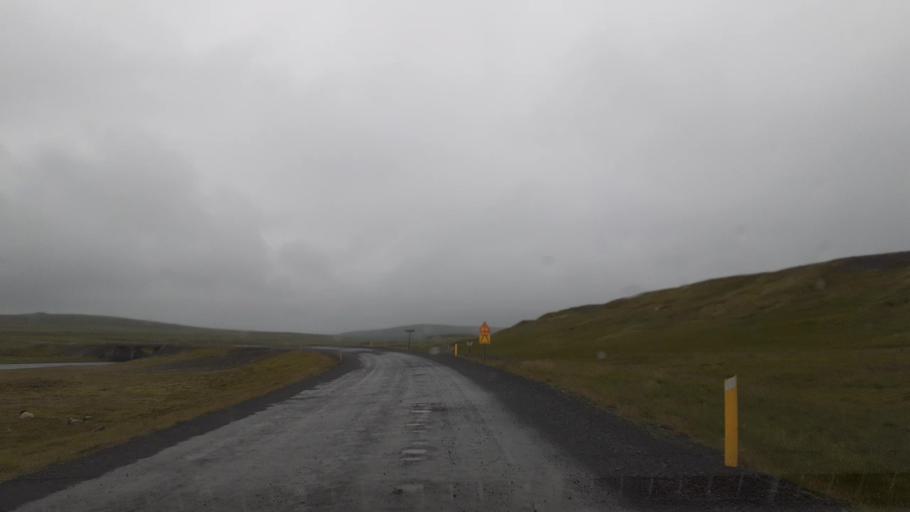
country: IS
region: East
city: Egilsstadir
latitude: 66.0424
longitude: -15.0983
